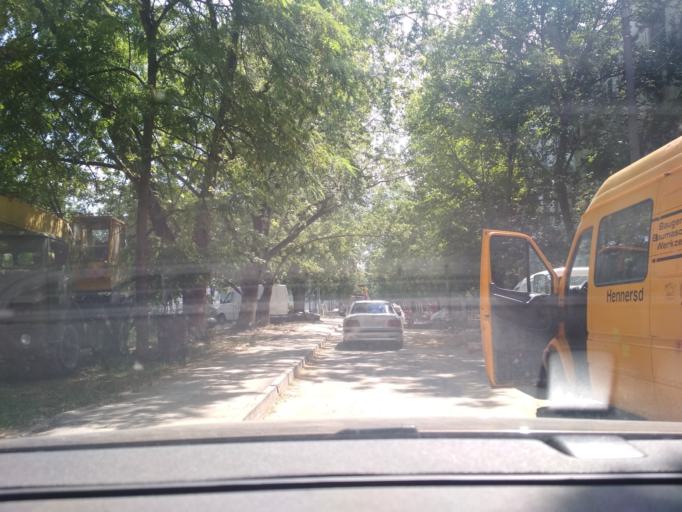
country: MD
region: Chisinau
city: Vatra
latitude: 47.0439
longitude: 28.7659
